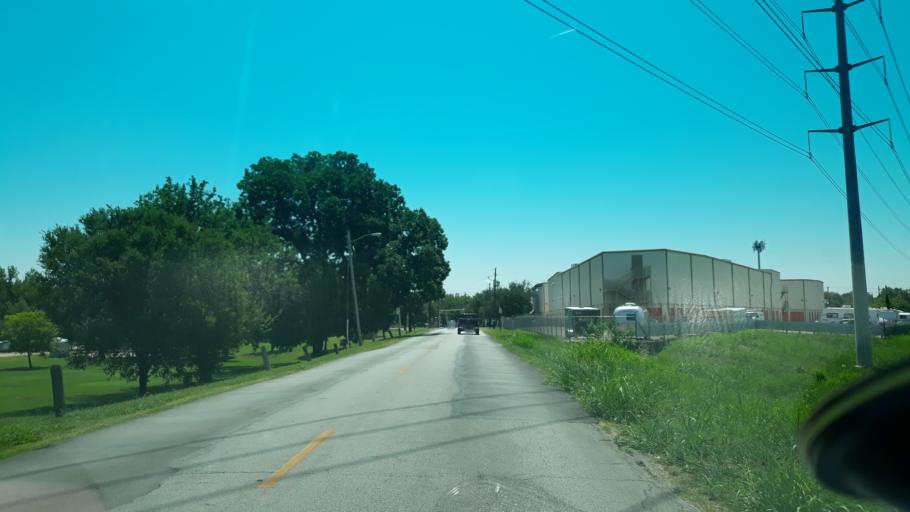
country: US
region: Texas
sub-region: Dallas County
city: Highland Park
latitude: 32.8145
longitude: -96.7288
